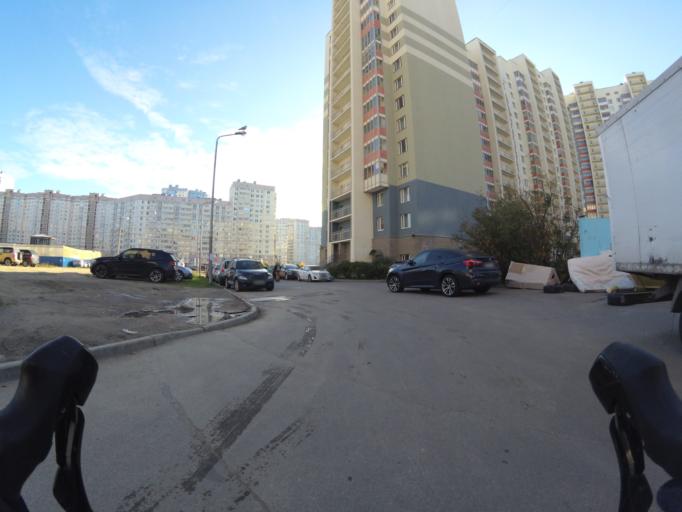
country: RU
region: Leningrad
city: Untolovo
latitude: 59.9977
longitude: 30.2055
